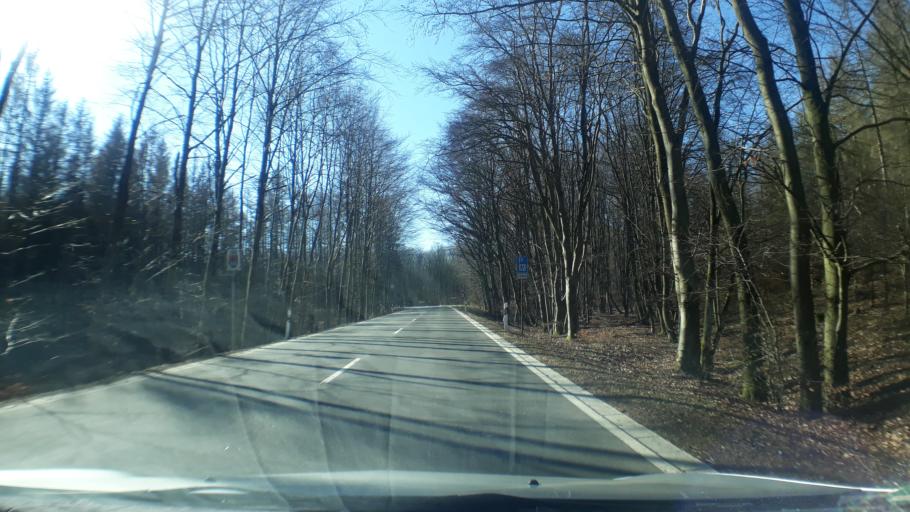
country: DE
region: North Rhine-Westphalia
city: Heimbach
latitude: 50.6169
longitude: 6.4395
